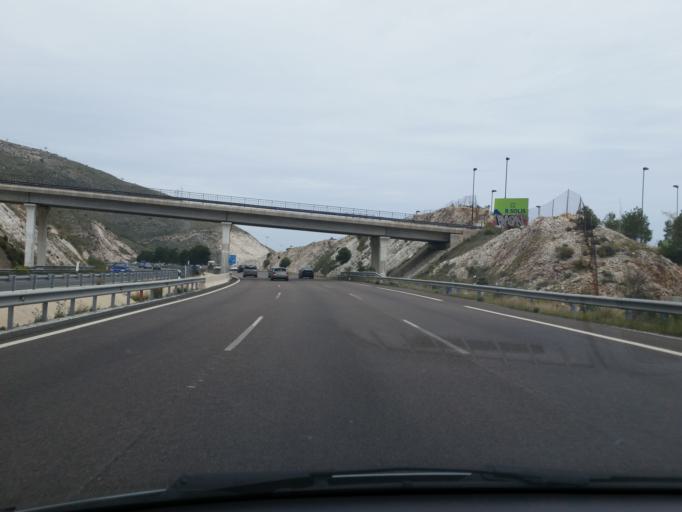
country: ES
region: Andalusia
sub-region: Provincia de Malaga
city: Benalmadena
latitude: 36.6049
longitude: -4.5627
